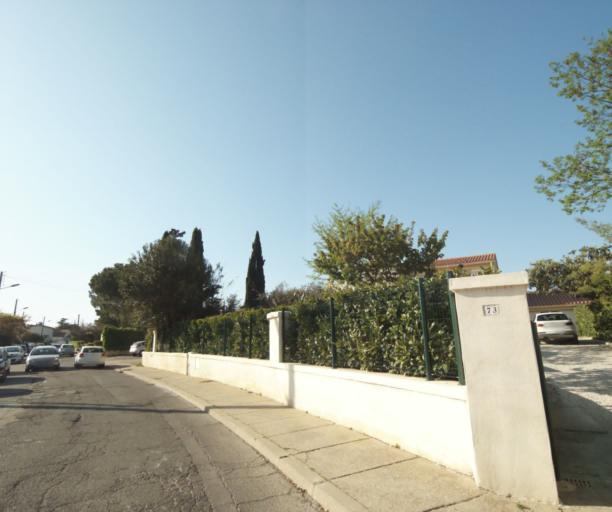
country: FR
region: Languedoc-Roussillon
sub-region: Departement de l'Herault
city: Castelnau-le-Lez
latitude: 43.6337
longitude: 3.9157
